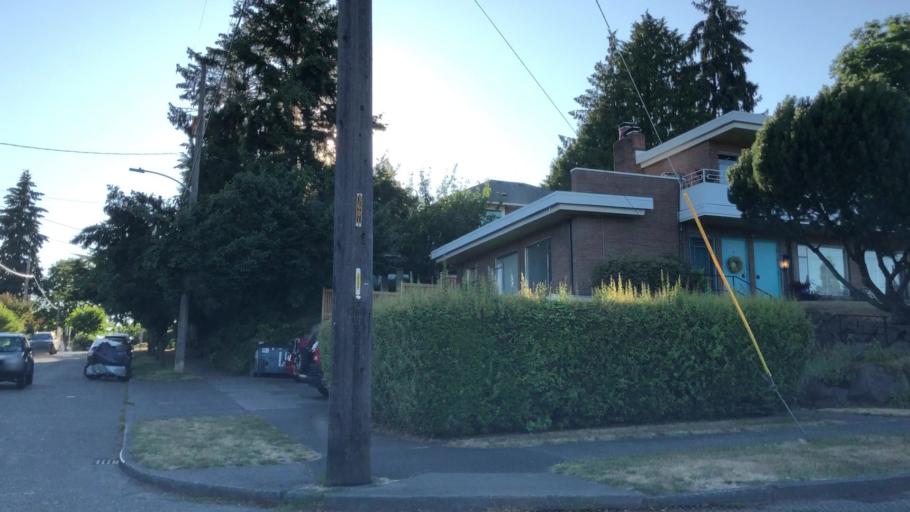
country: US
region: Washington
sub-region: King County
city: Seattle
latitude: 47.6505
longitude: -122.3338
